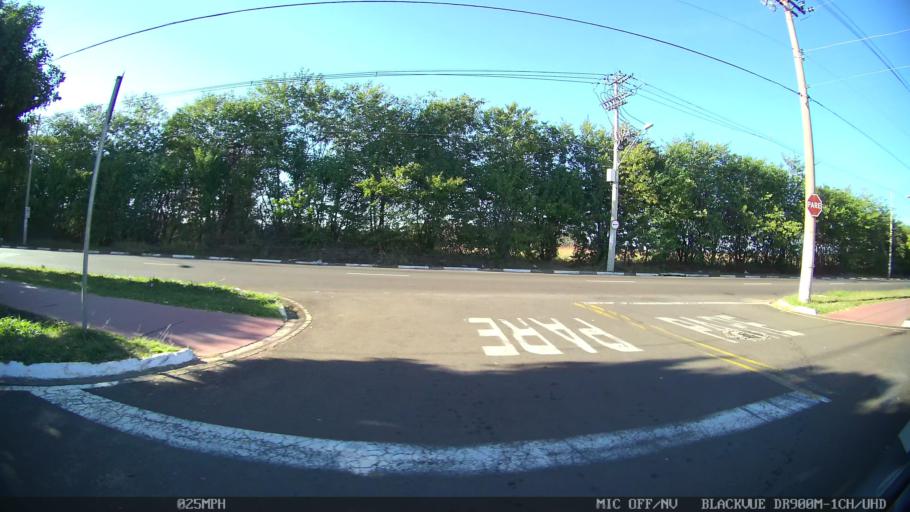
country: BR
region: Sao Paulo
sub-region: Franca
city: Franca
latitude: -20.5709
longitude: -47.3680
